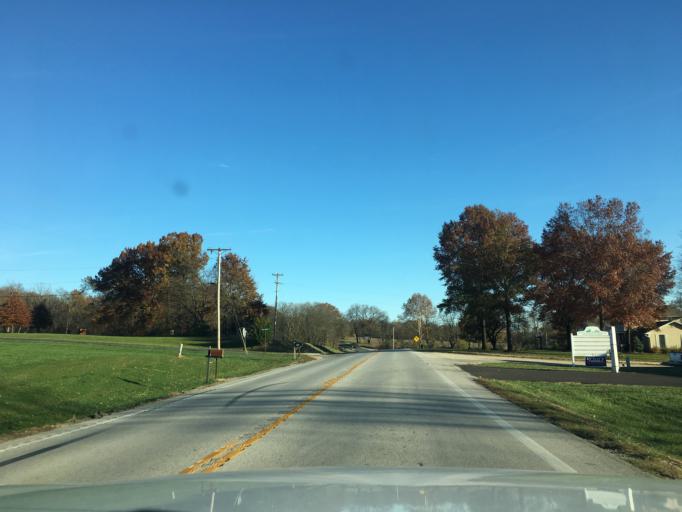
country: US
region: Missouri
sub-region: Franklin County
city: New Haven
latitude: 38.6002
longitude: -91.2564
